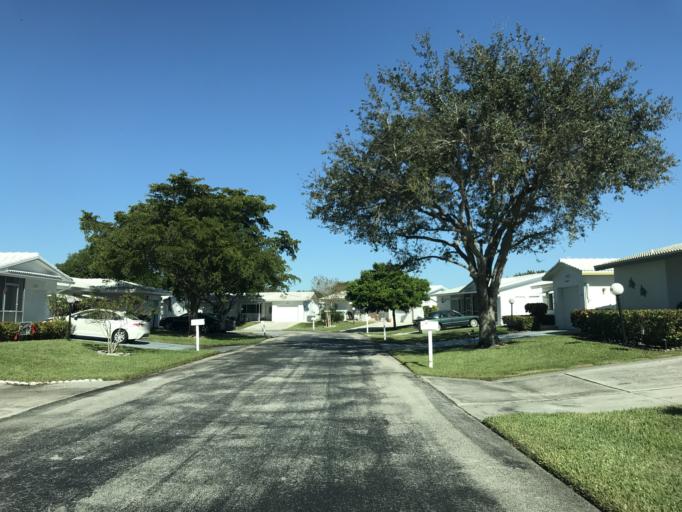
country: US
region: Florida
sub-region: Broward County
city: Plantation
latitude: 26.1377
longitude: -80.2675
